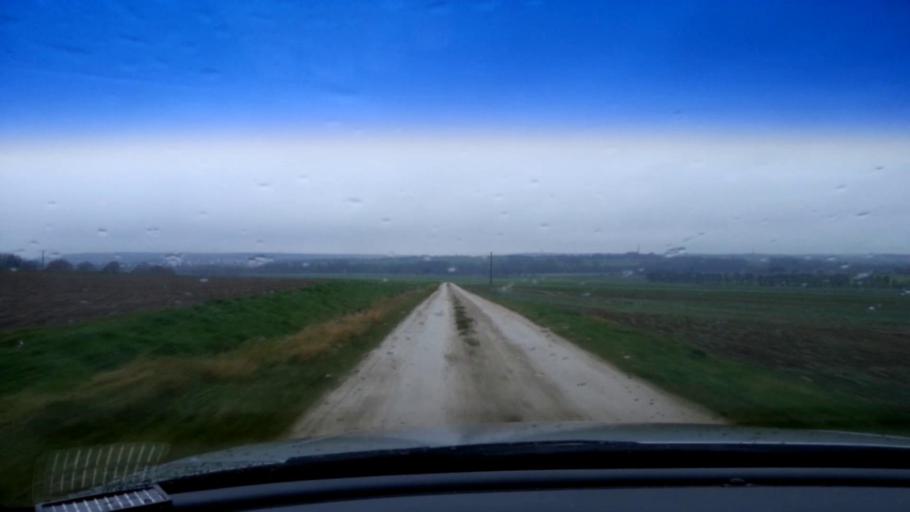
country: DE
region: Bavaria
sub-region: Upper Franconia
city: Litzendorf
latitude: 49.9451
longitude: 11.0076
